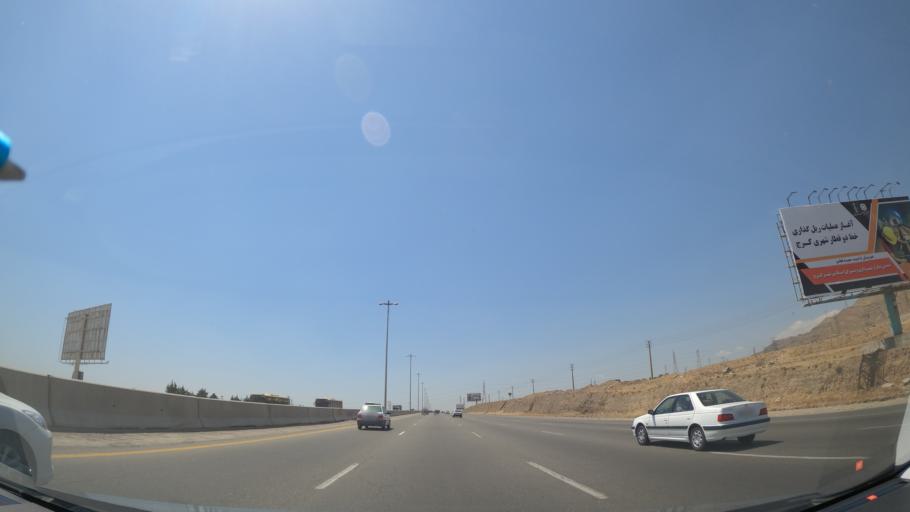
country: IR
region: Tehran
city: Shahr-e Qods
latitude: 35.7673
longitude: 51.0522
